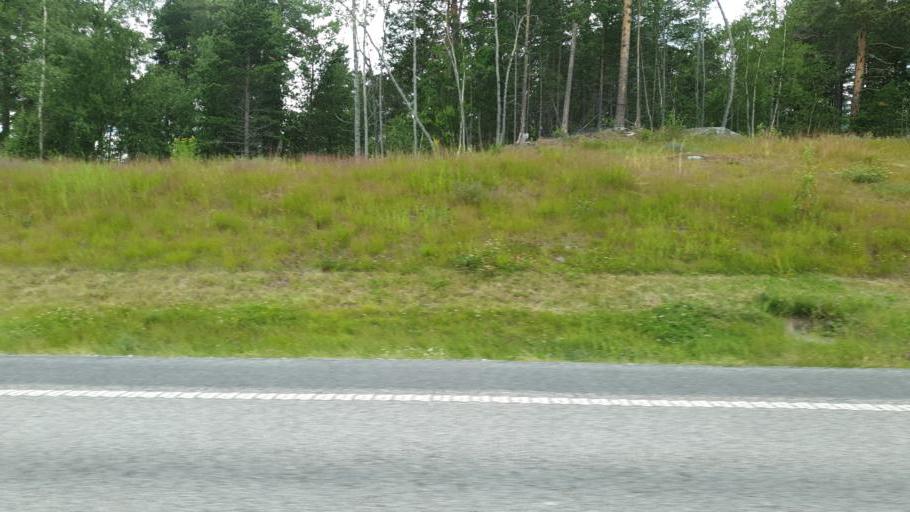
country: NO
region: Sor-Trondelag
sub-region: Oppdal
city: Oppdal
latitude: 62.5814
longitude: 9.6704
